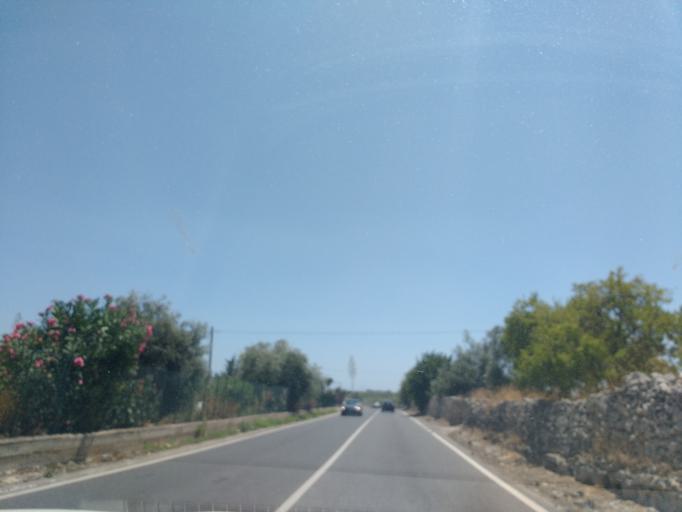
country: IT
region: Sicily
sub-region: Provincia di Siracusa
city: Noto
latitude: 36.8775
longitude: 15.0470
